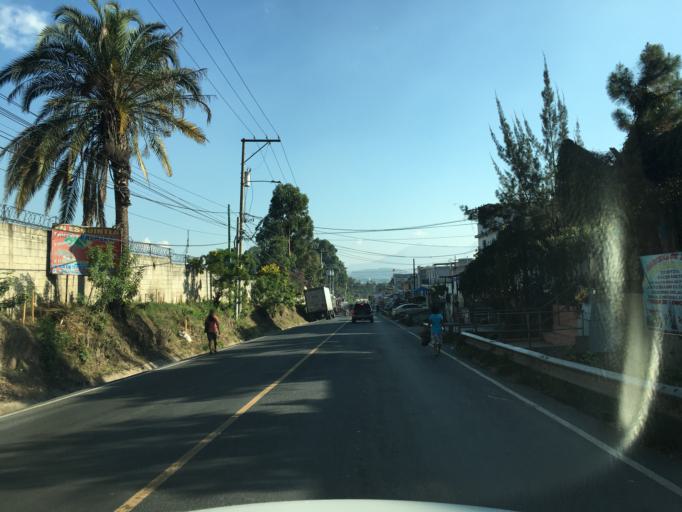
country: GT
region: Guatemala
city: Villa Nueva
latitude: 14.5426
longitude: -90.6161
